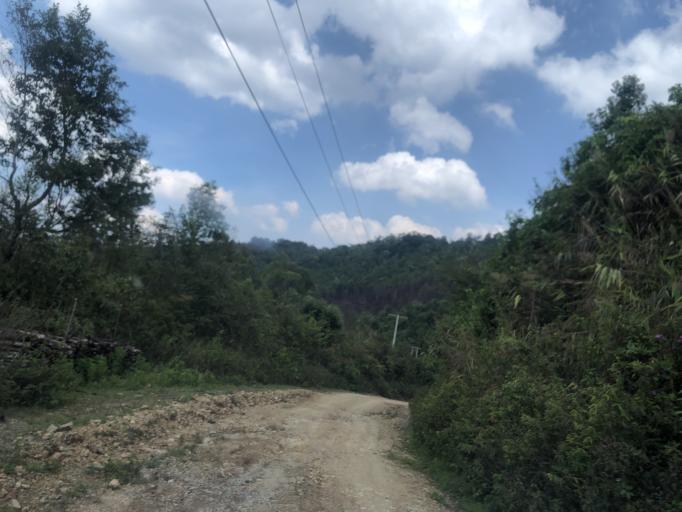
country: LA
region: Phongsali
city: Phongsali
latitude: 21.3911
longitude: 102.2019
